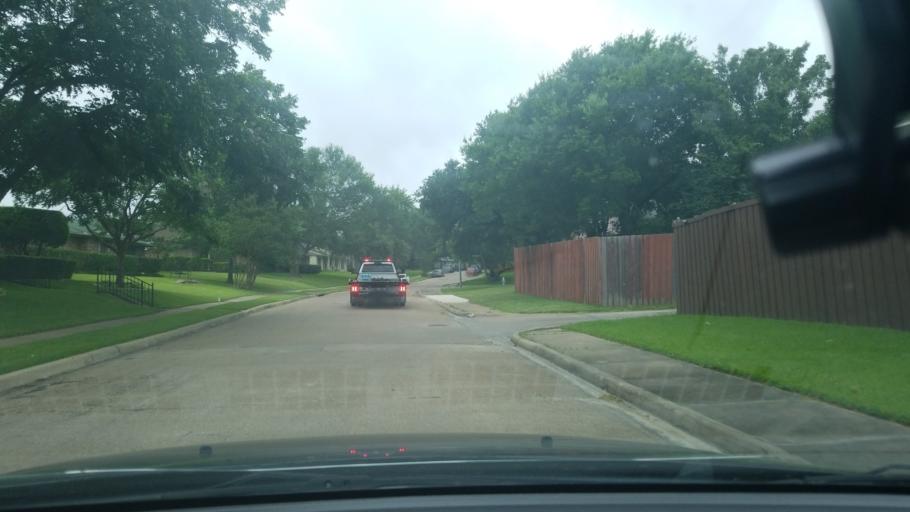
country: US
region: Texas
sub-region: Dallas County
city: Mesquite
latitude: 32.7808
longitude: -96.6312
